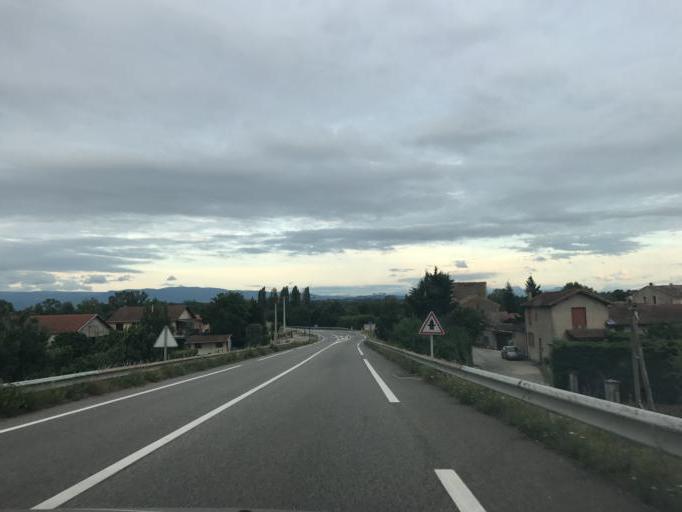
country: FR
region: Rhone-Alpes
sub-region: Departement de l'Ardeche
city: Charmes-sur-Rhone
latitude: 44.8557
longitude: 4.8333
